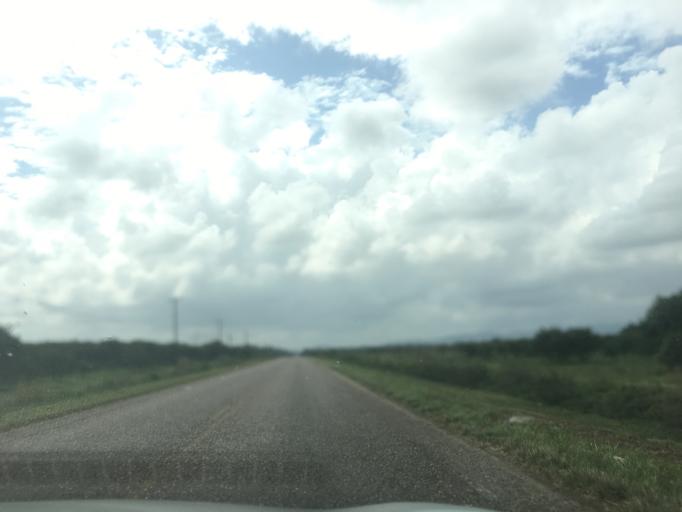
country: BZ
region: Stann Creek
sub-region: Dangriga
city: Dangriga
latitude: 16.9769
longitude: -88.2981
